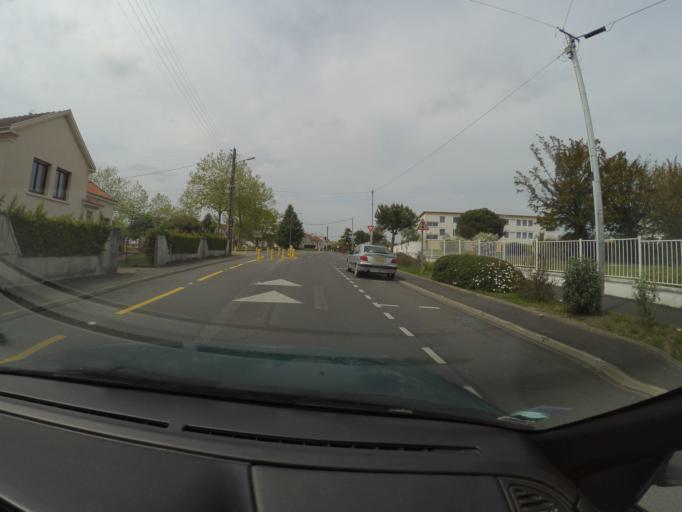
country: FR
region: Pays de la Loire
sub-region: Departement de la Loire-Atlantique
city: Clisson
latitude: 47.0915
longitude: -1.2891
